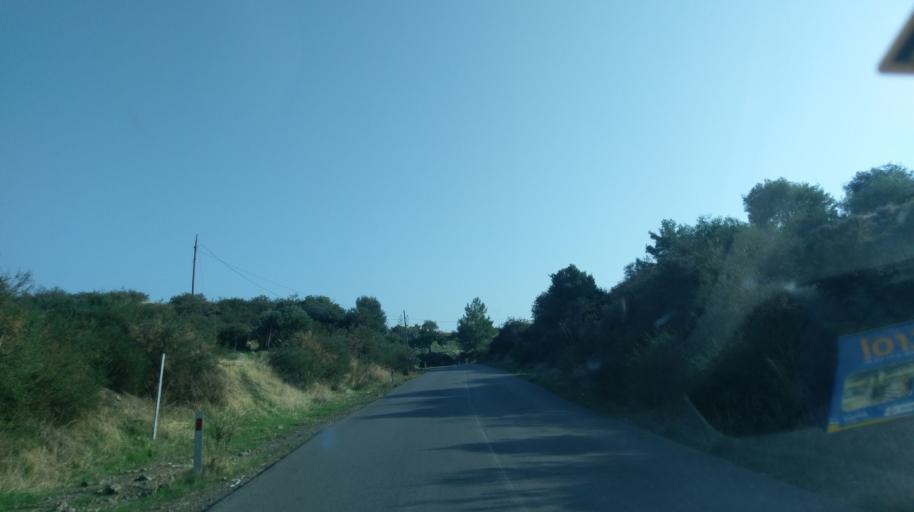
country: CY
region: Lefkosia
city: Kato Pyrgos
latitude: 35.1589
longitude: 32.7555
